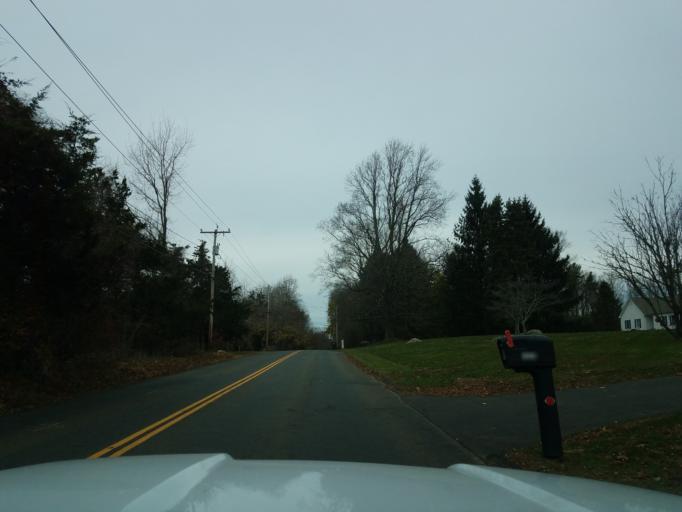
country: US
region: Connecticut
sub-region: New Haven County
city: Guilford
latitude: 41.3205
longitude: -72.7113
